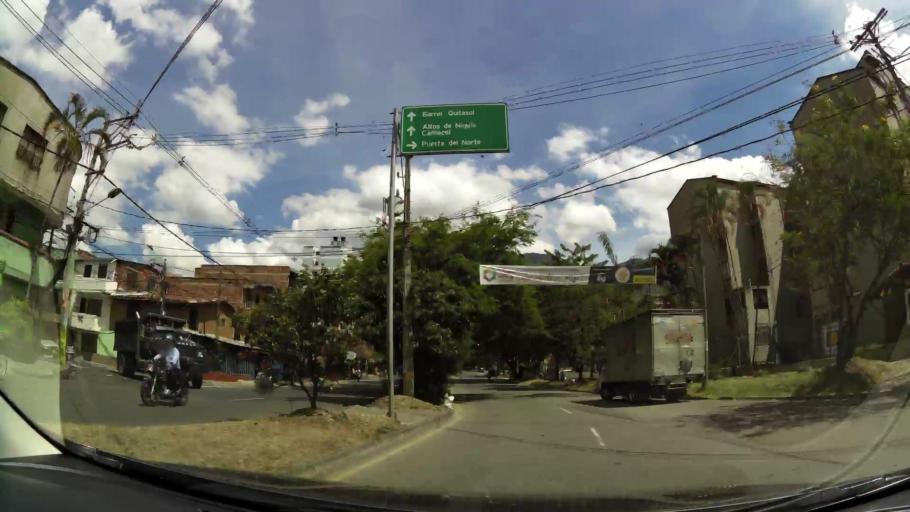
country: CO
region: Antioquia
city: Bello
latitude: 6.3383
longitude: -75.5480
